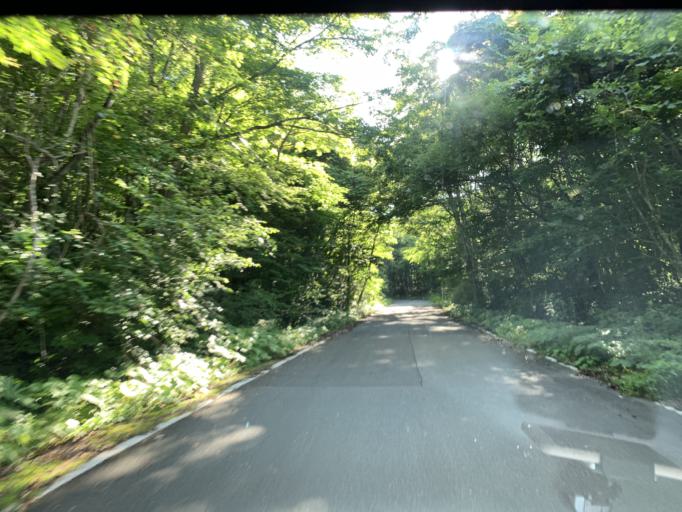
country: JP
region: Iwate
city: Ichinoseki
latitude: 38.9155
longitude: 140.8283
